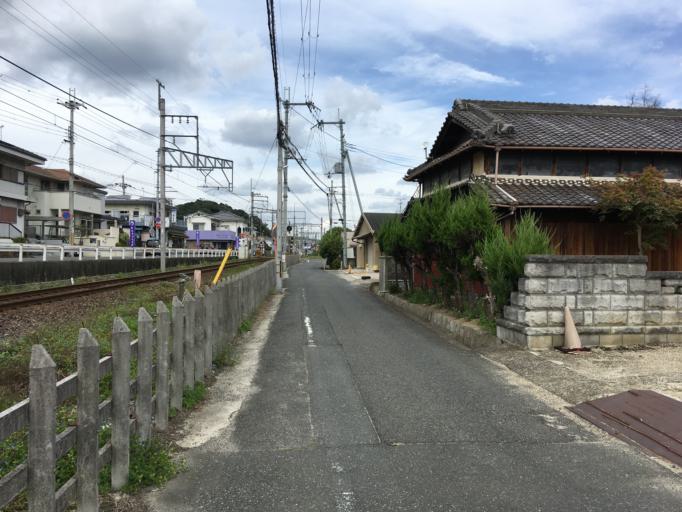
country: JP
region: Nara
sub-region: Ikoma-shi
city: Ikoma
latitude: 34.6186
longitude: 135.7047
